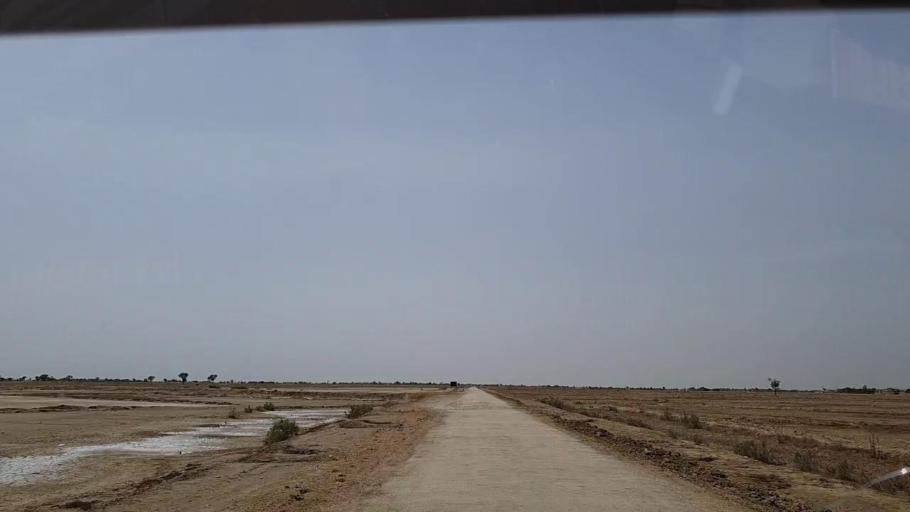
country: PK
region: Sindh
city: Johi
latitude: 26.7436
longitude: 67.6291
